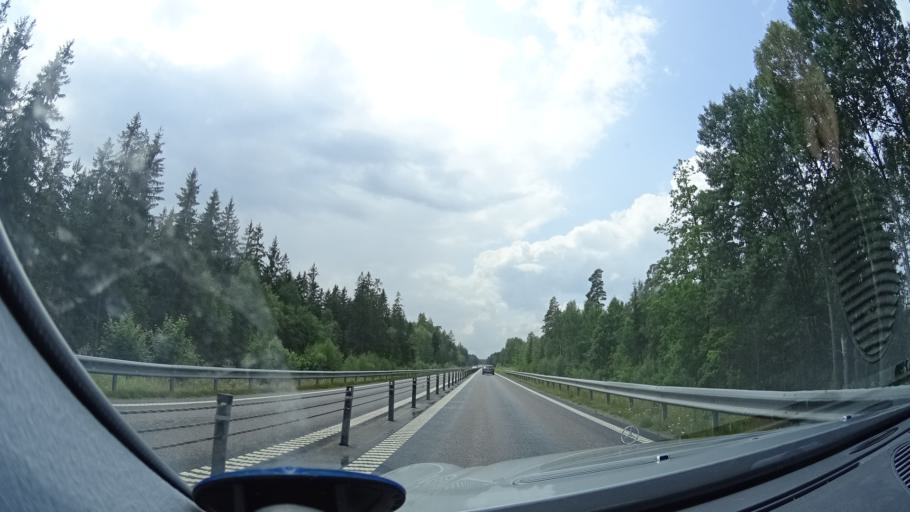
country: SE
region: Kalmar
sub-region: Nybro Kommun
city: Nybro
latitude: 56.7174
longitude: 15.7827
